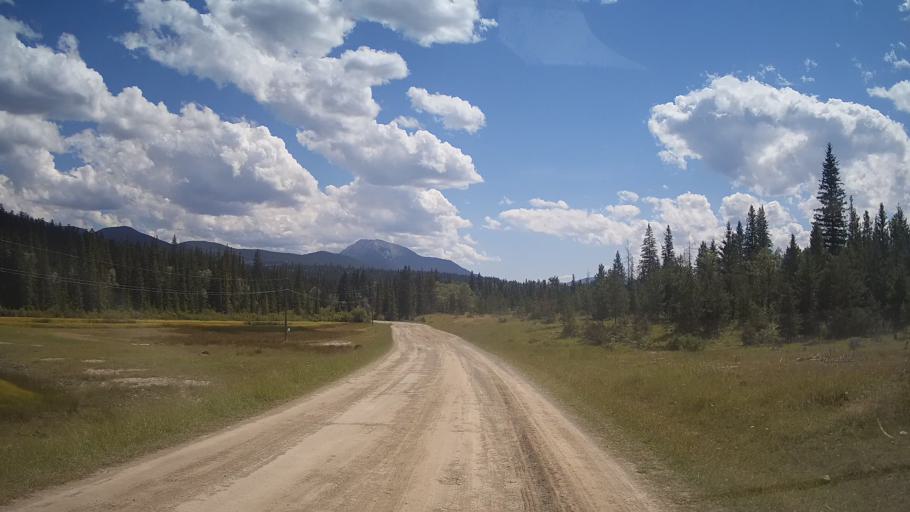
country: CA
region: British Columbia
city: Lillooet
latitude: 51.2952
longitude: -121.9809
